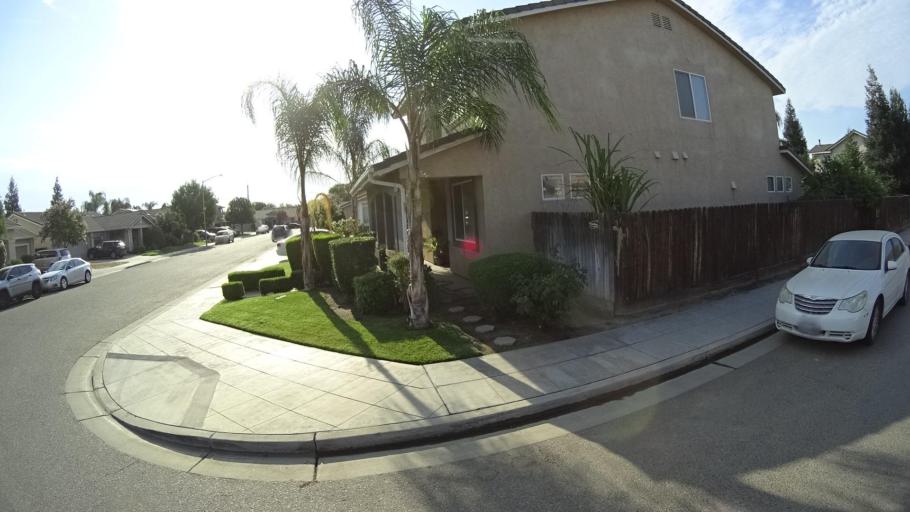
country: US
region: California
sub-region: Fresno County
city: Sunnyside
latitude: 36.7110
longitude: -119.6928
